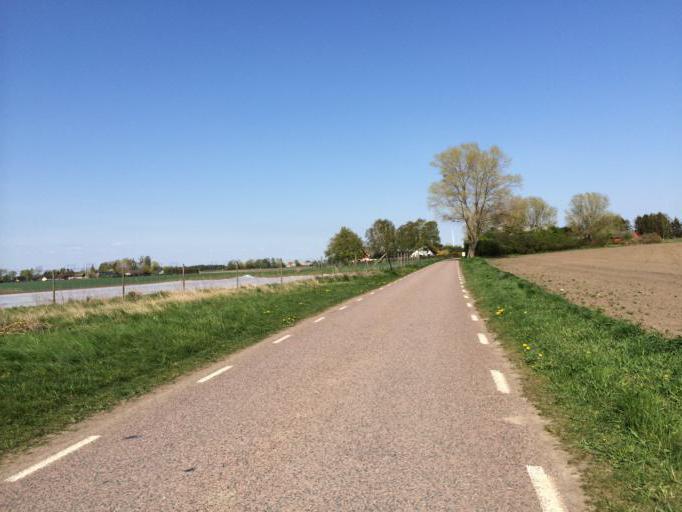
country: SE
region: Skane
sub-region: Kavlinge Kommun
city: Loddekopinge
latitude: 55.7933
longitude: 13.0385
